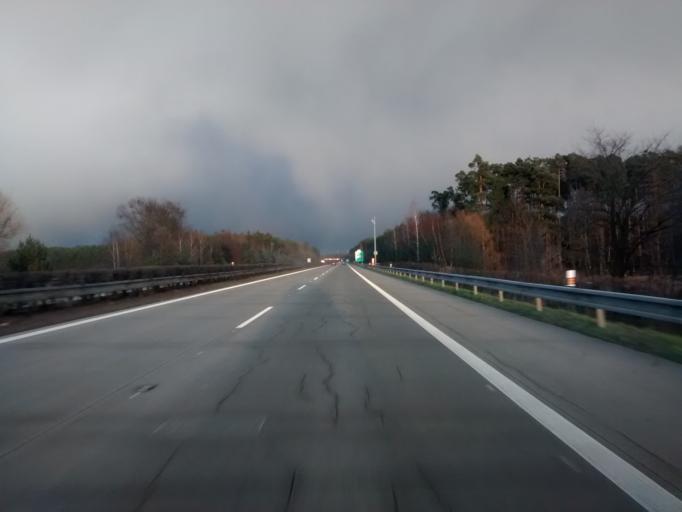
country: CZ
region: Central Bohemia
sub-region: Okres Nymburk
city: Podebrady
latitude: 50.1197
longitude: 15.1074
